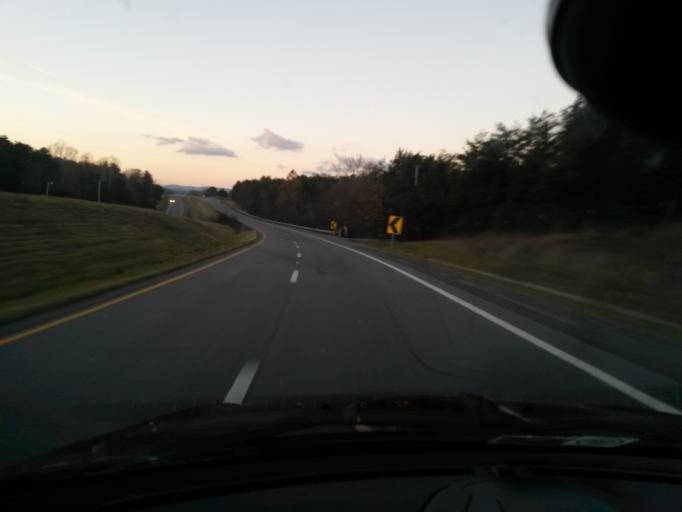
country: US
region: Virginia
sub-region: Botetourt County
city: Fincastle
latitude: 37.5524
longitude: -79.8541
